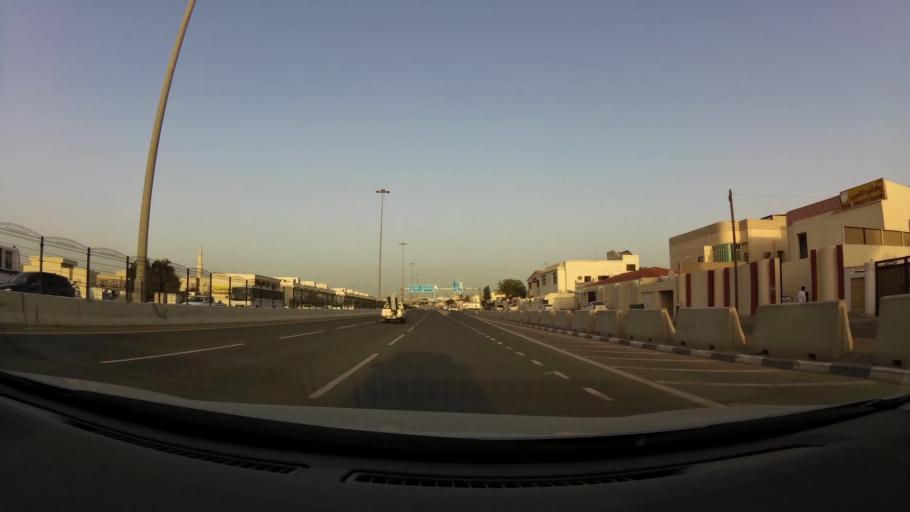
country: QA
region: Baladiyat ar Rayyan
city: Ar Rayyan
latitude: 25.3201
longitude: 51.4640
